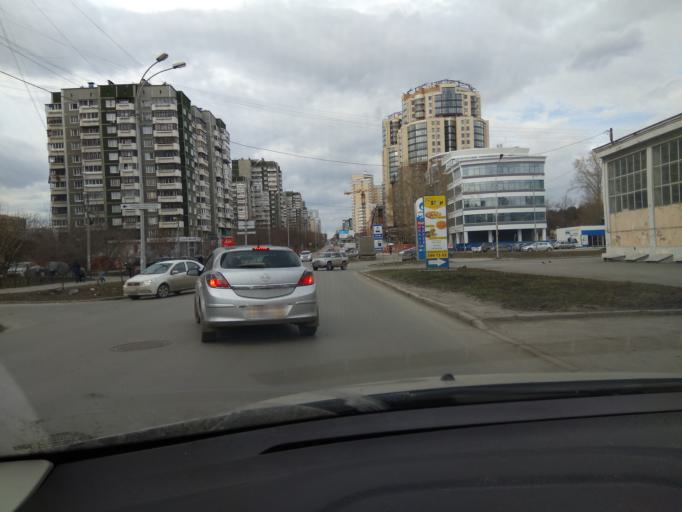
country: RU
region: Sverdlovsk
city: Yekaterinburg
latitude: 56.8170
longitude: 60.5918
